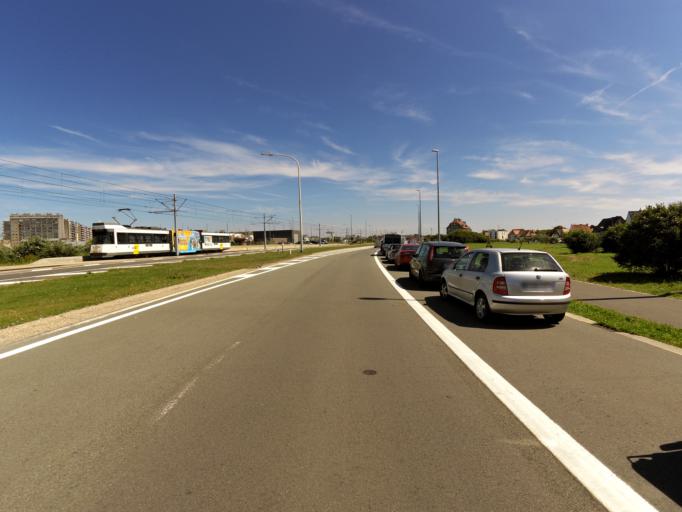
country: BE
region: Flanders
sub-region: Provincie West-Vlaanderen
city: Blankenberge
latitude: 51.3103
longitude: 3.1102
